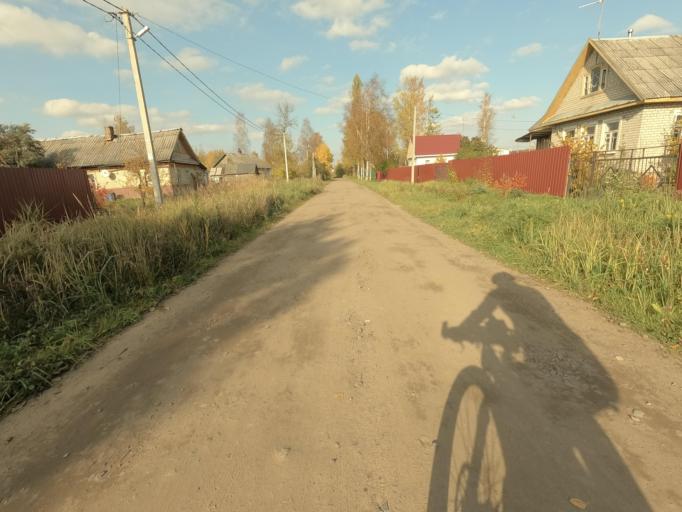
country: RU
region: Leningrad
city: Mga
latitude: 59.7510
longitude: 31.0732
